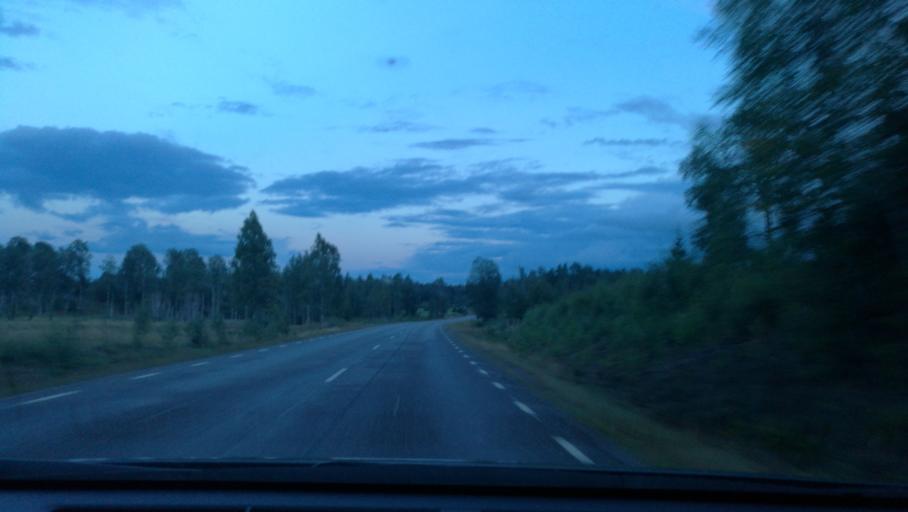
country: SE
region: OEstergoetland
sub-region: Norrkopings Kommun
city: Svartinge
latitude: 58.7819
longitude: 15.9664
